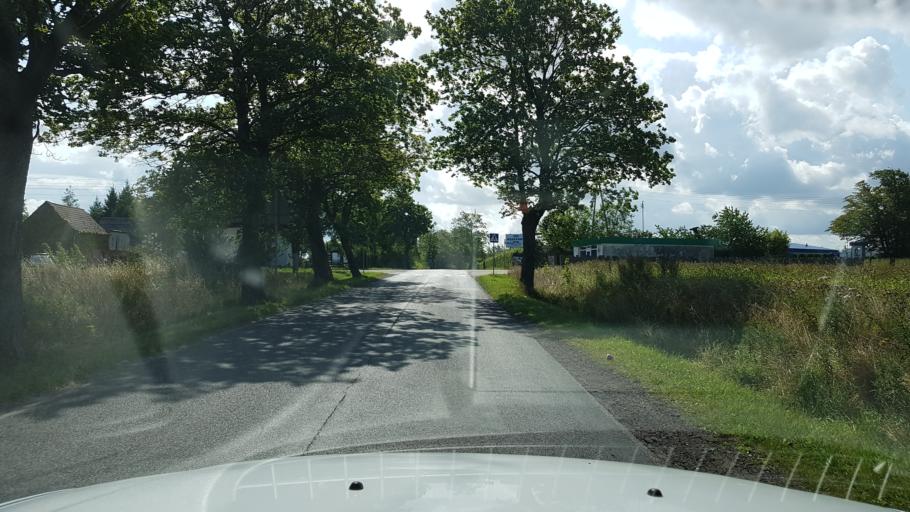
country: PL
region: West Pomeranian Voivodeship
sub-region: Powiat kolobrzeski
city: Ustronie Morskie
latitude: 54.1829
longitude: 15.7437
